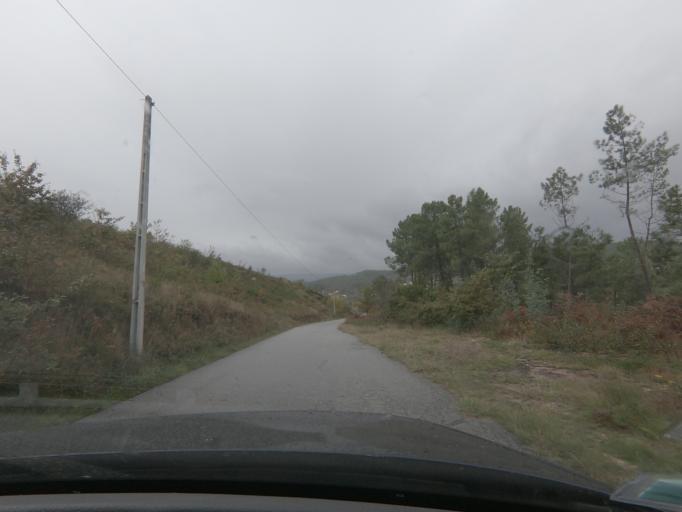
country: PT
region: Vila Real
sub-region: Mondim de Basto
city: Mondim de Basto
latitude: 41.3735
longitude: -7.9446
